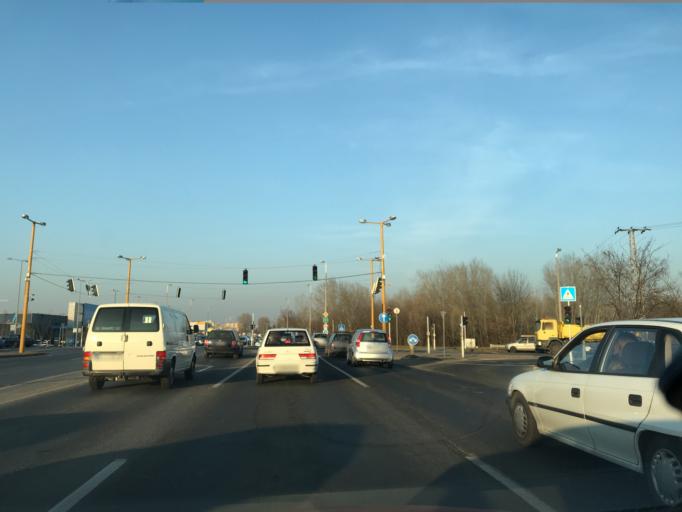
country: HU
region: Gyor-Moson-Sopron
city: Gyor
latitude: 47.6537
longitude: 17.6317
